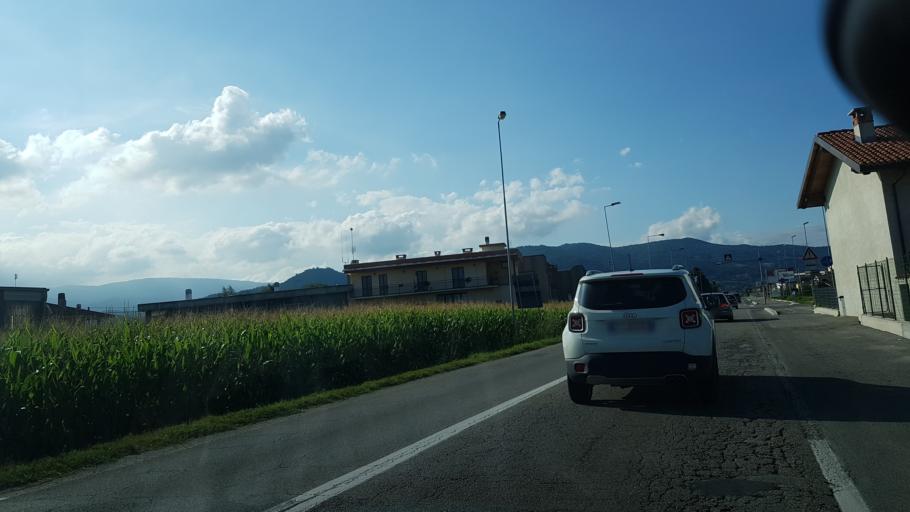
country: IT
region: Piedmont
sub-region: Provincia di Cuneo
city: Busca
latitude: 44.4997
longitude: 7.4921
